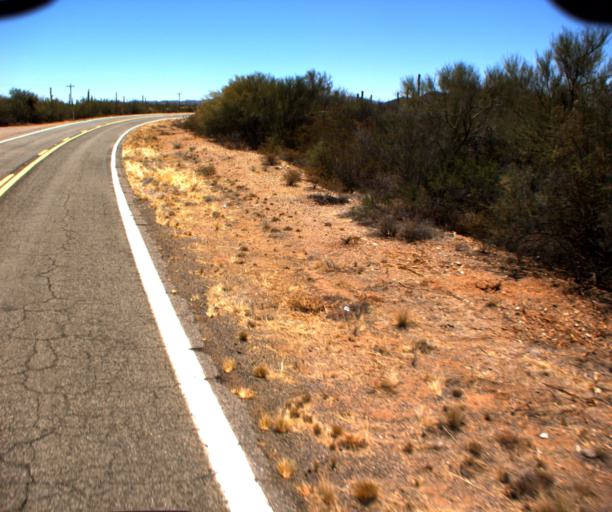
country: US
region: Arizona
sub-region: Pima County
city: Sells
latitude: 32.1819
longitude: -112.2818
